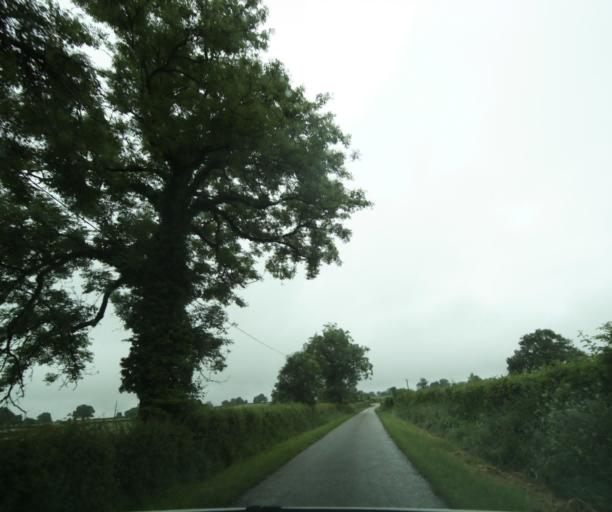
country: FR
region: Bourgogne
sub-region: Departement de Saone-et-Loire
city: Charolles
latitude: 46.4712
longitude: 4.2241
